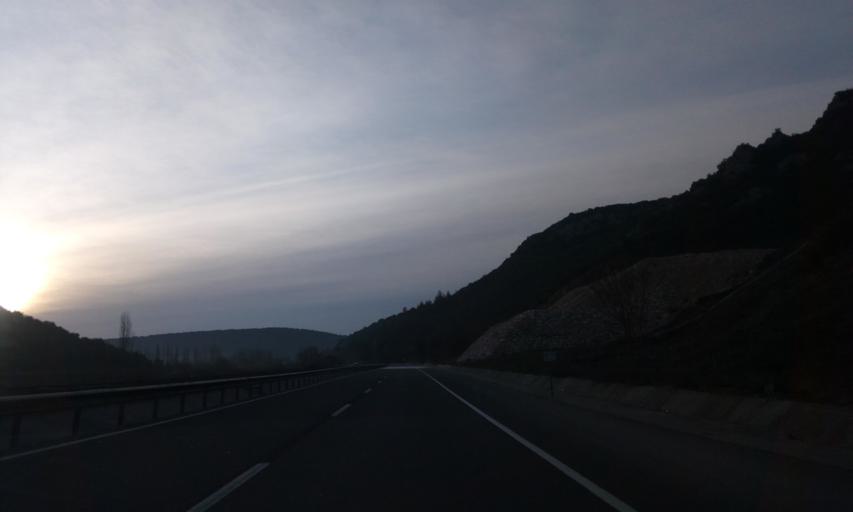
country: TR
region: Bilecik
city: Bilecik
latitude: 40.1531
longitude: 30.0208
